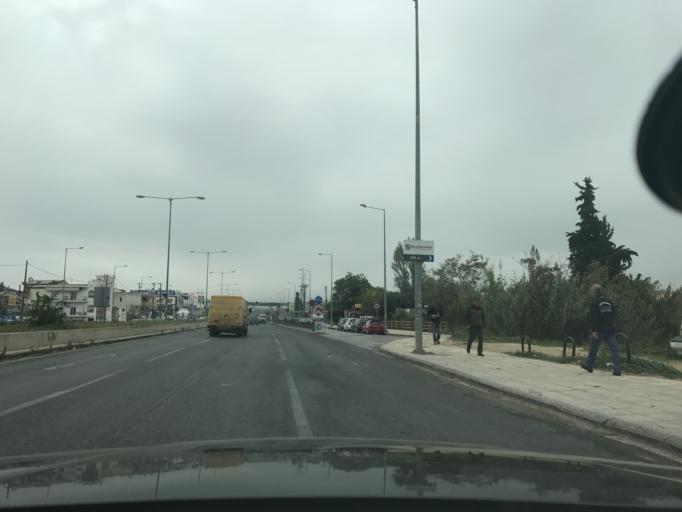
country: GR
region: Central Macedonia
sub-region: Nomos Thessalonikis
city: Stavroupoli
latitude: 40.6727
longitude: 22.9390
